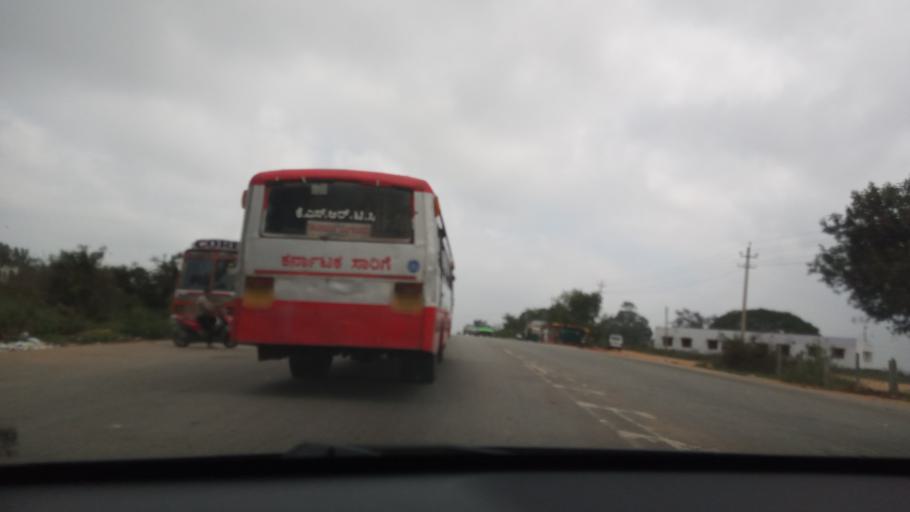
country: IN
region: Karnataka
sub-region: Chikkaballapur
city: Chintamani
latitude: 13.3593
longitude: 78.0388
